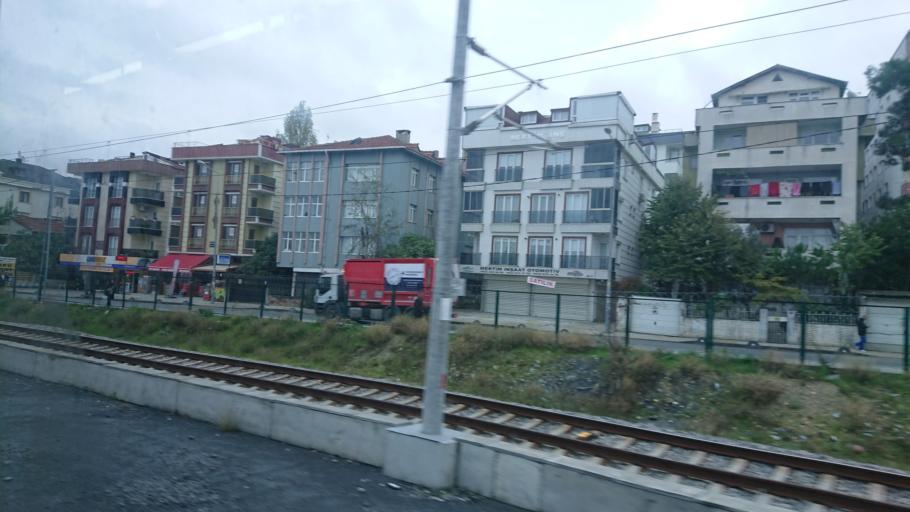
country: TR
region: Istanbul
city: Mahmutbey
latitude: 41.0077
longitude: 28.7746
